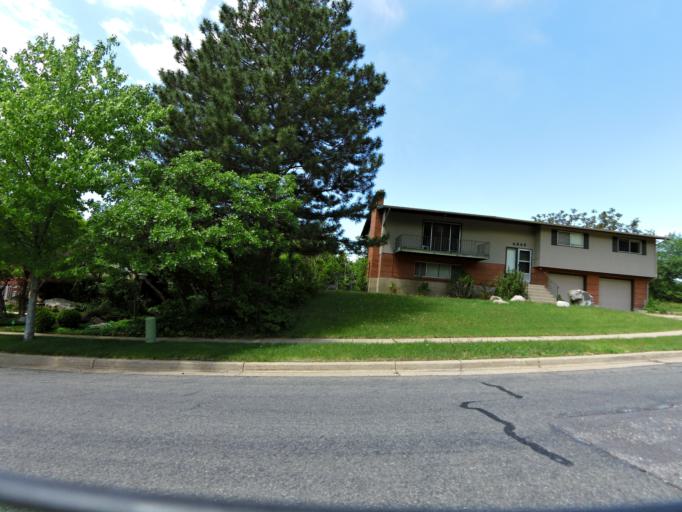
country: US
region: Utah
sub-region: Weber County
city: Uintah
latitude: 41.1749
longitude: -111.9294
